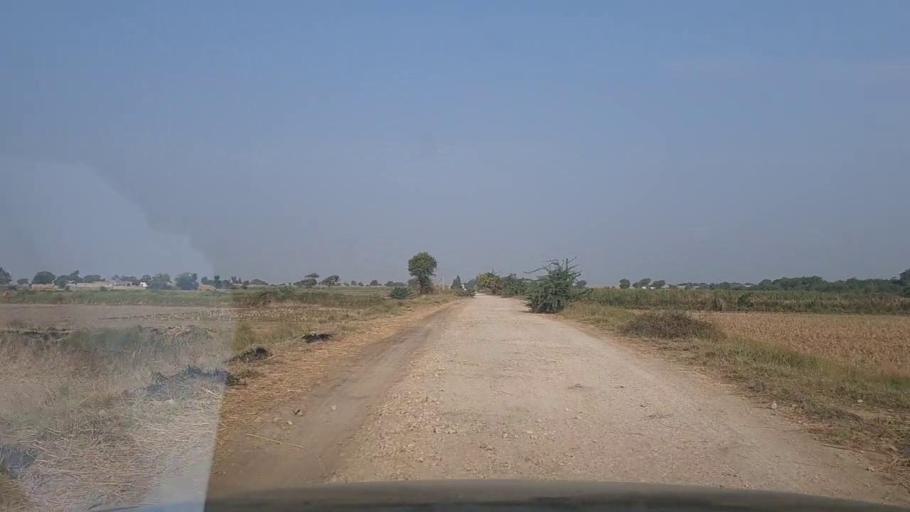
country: PK
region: Sindh
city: Bulri
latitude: 24.9378
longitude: 68.2825
